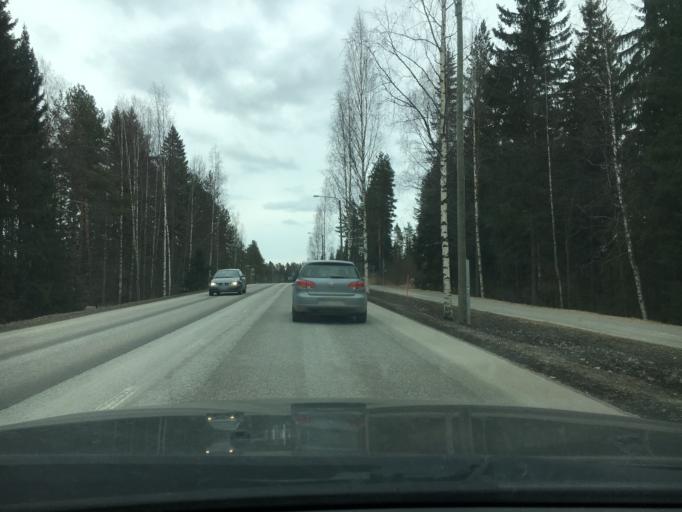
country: FI
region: Central Finland
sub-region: AEaenekoski
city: Suolahti
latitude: 62.5596
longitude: 25.8681
